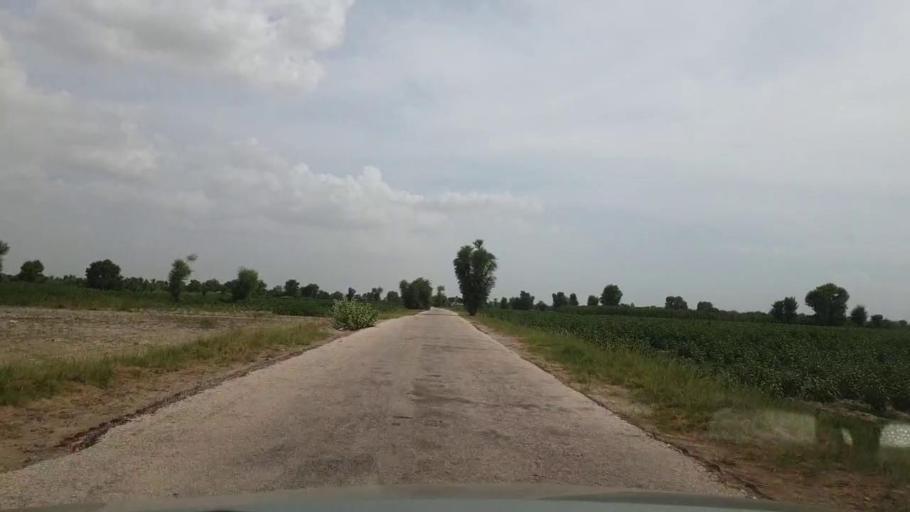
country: PK
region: Sindh
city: Kot Diji
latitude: 27.1421
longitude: 69.0281
